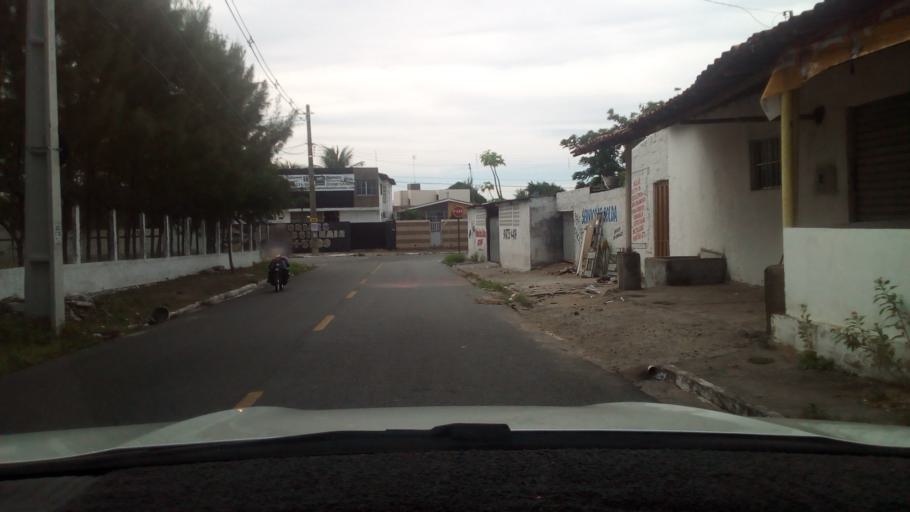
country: BR
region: Paraiba
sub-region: Joao Pessoa
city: Joao Pessoa
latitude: -7.1645
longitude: -34.8635
